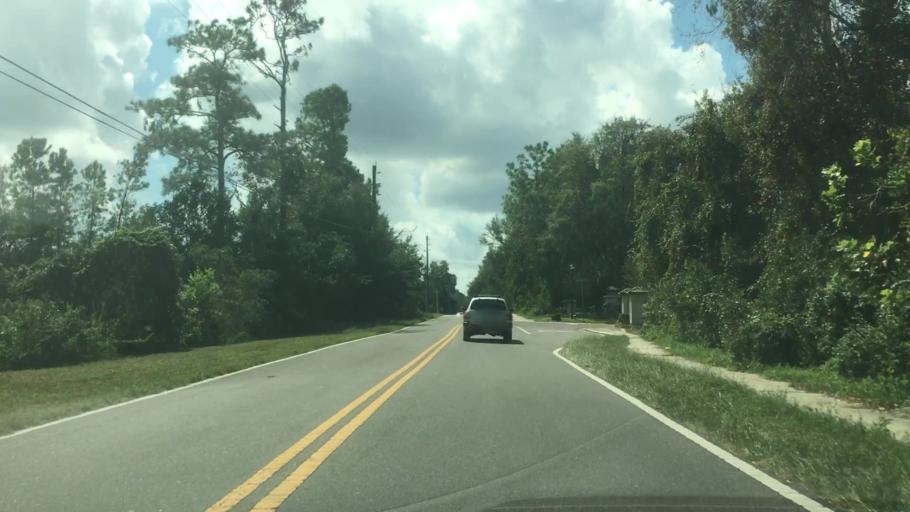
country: US
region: Florida
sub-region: Duval County
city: Jacksonville
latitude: 30.4506
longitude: -81.5791
